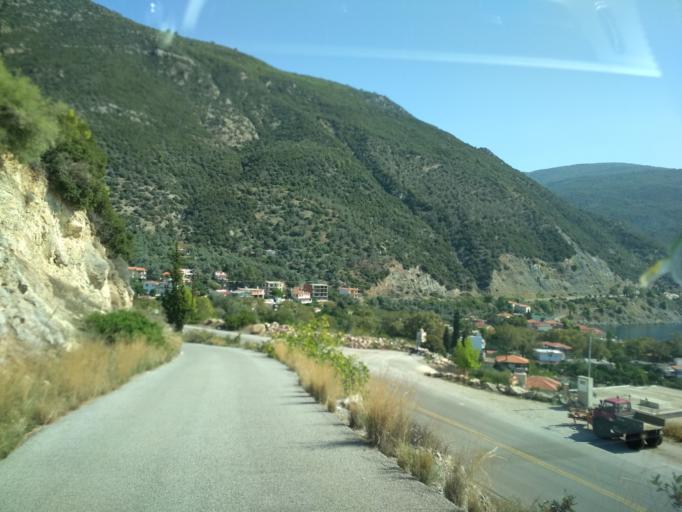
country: GR
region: Central Greece
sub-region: Nomos Evvoias
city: Oreoi
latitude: 38.8495
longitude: 23.1227
